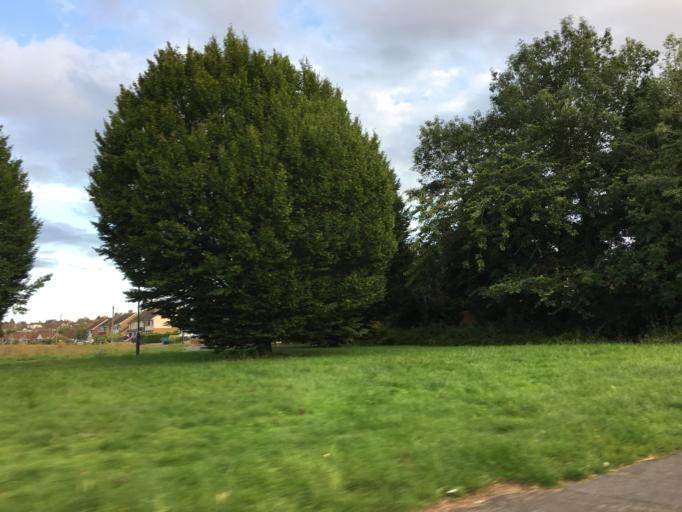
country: GB
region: England
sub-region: Warwickshire
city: Rugby
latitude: 52.3589
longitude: -1.2792
